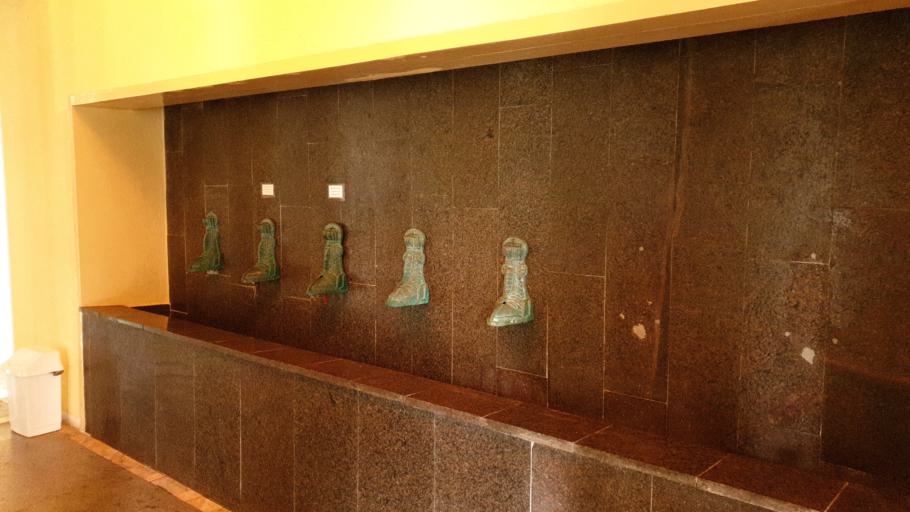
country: LT
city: Birstonas
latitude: 54.6016
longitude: 24.0294
